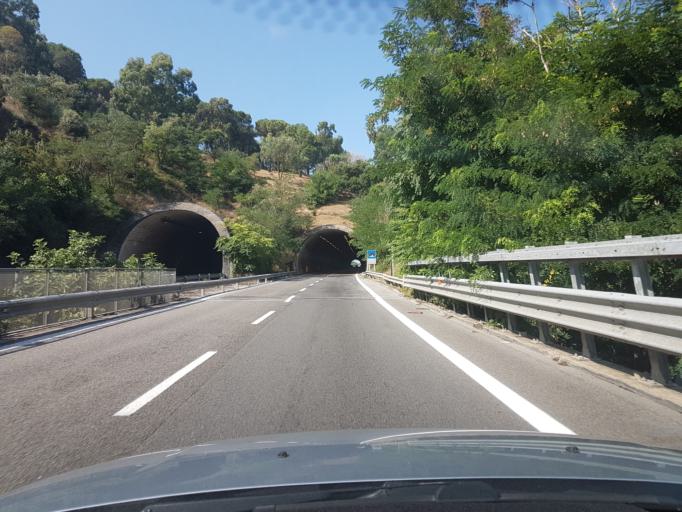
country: IT
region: Sardinia
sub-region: Provincia di Nuoro
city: Nuoro
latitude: 40.3304
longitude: 9.2912
